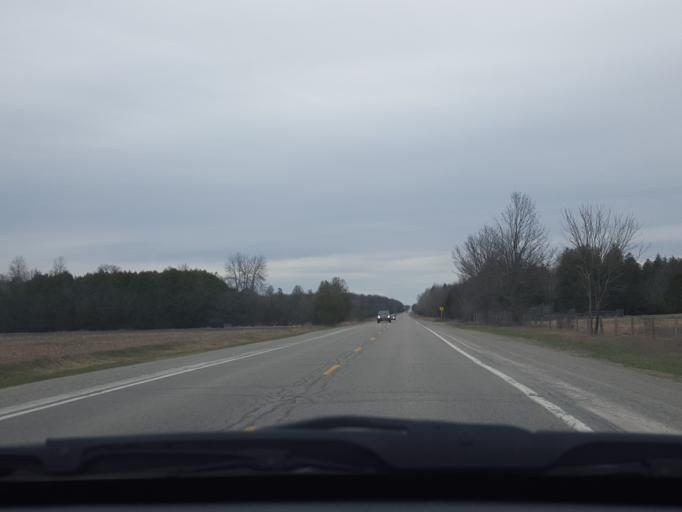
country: CA
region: Ontario
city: Uxbridge
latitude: 44.2856
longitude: -79.1659
